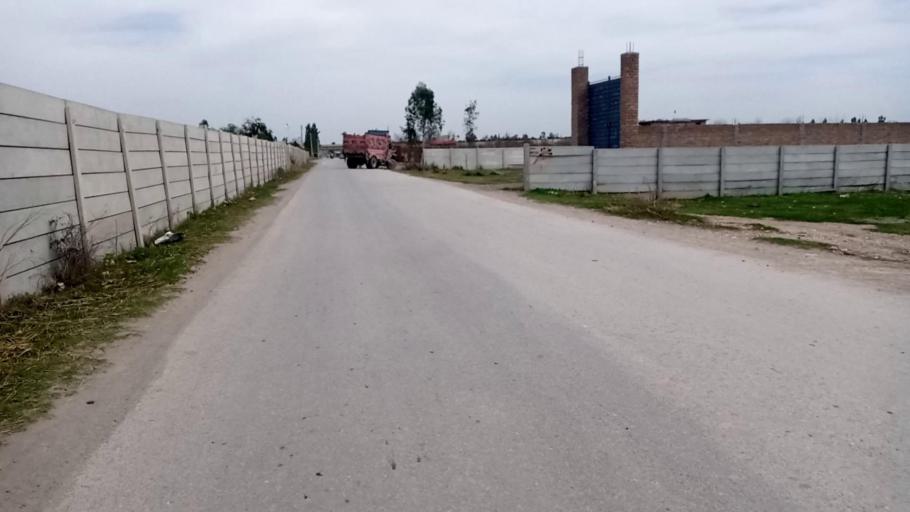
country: PK
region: Khyber Pakhtunkhwa
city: Charsadda
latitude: 34.0619
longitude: 71.7012
